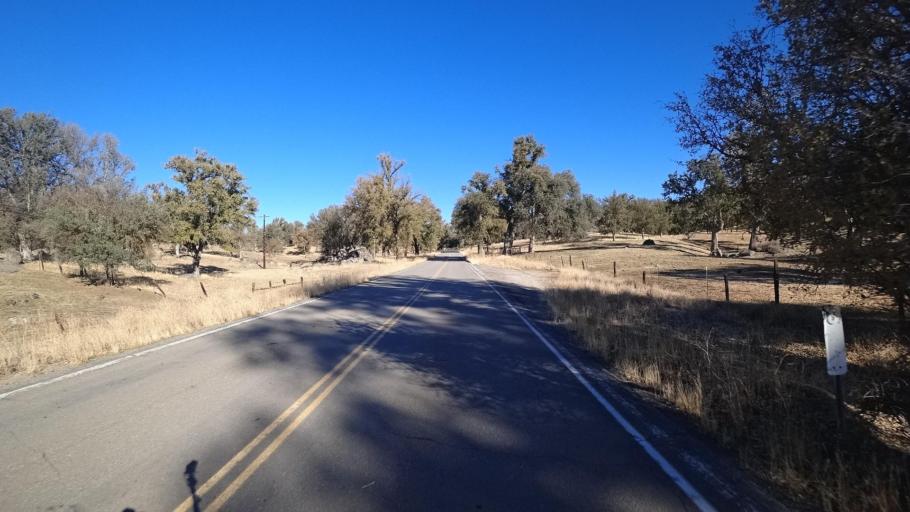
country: US
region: California
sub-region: Kern County
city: Alta Sierra
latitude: 35.7458
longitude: -118.7176
